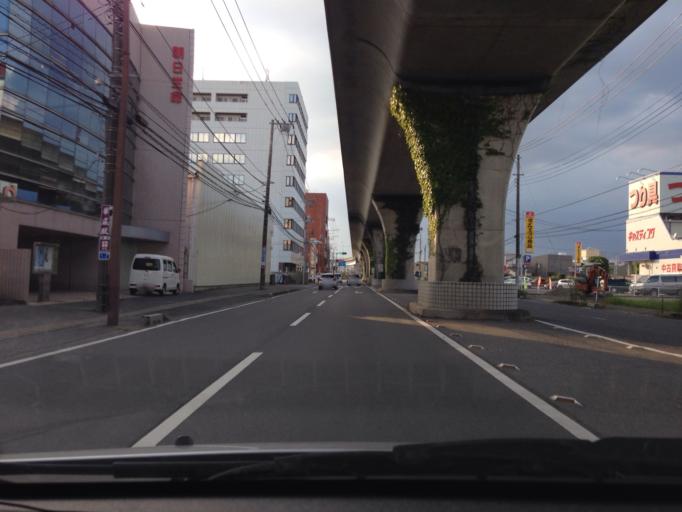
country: JP
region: Ibaraki
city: Naka
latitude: 36.0862
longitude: 140.1867
